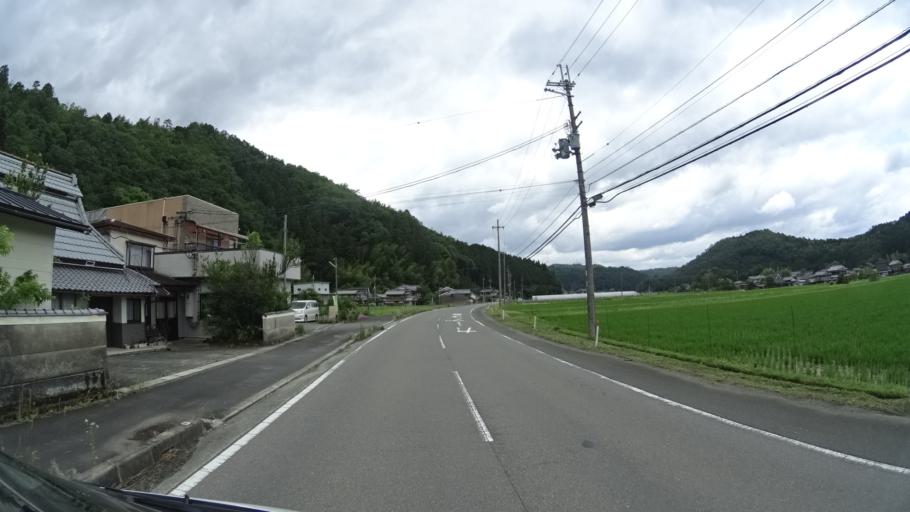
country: JP
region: Kyoto
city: Kameoka
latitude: 35.0968
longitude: 135.4325
